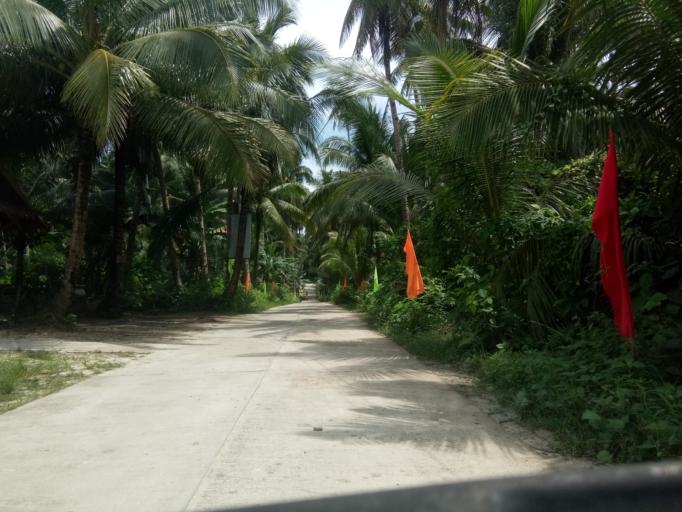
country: PH
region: Caraga
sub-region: Province of Surigao del Norte
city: Pilar
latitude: 9.8755
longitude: 126.1171
